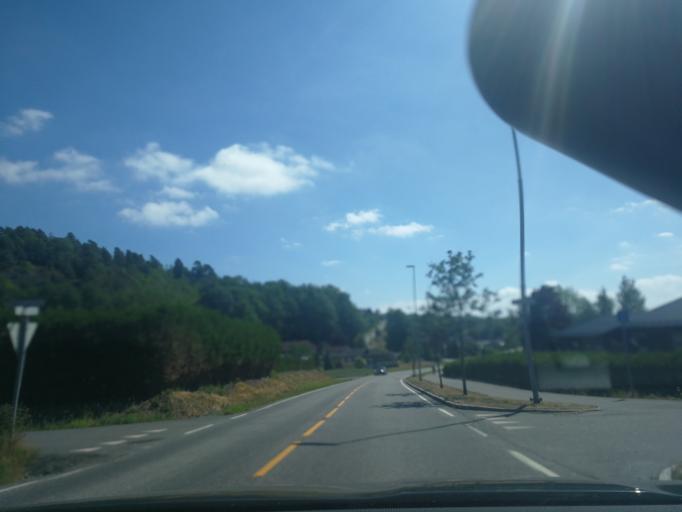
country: NO
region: Vestfold
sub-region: Stokke
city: Melsomvik
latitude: 59.2284
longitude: 10.3285
